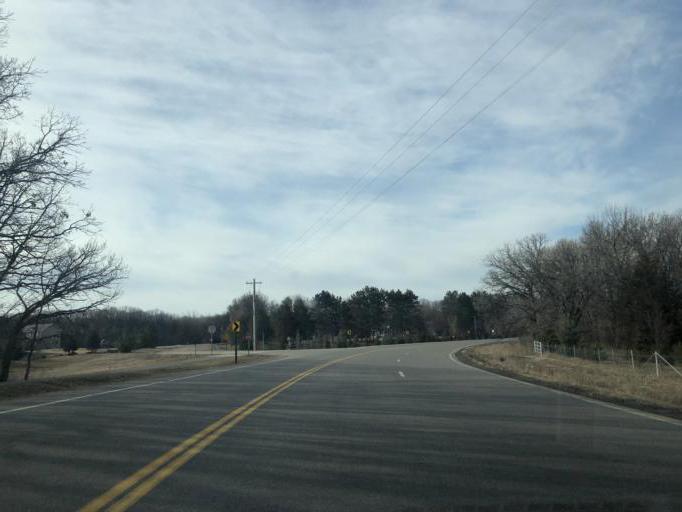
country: US
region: Minnesota
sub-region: Sherburne County
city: Becker
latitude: 45.3961
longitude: -93.8497
